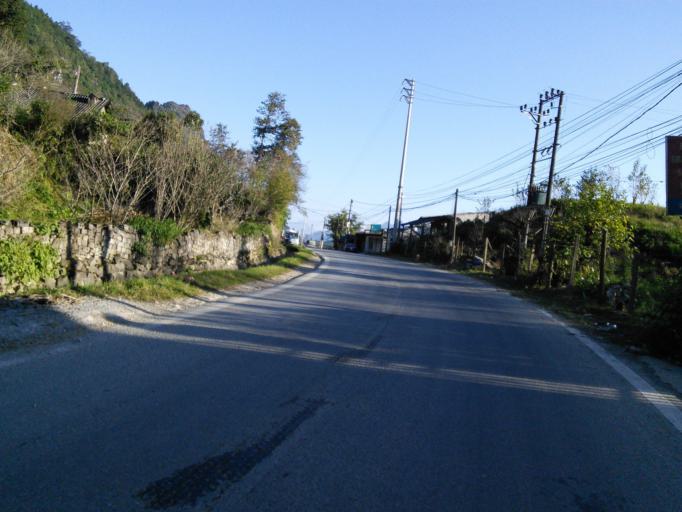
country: VN
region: Lao Cai
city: Sa Pa
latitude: 22.3671
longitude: 103.8026
